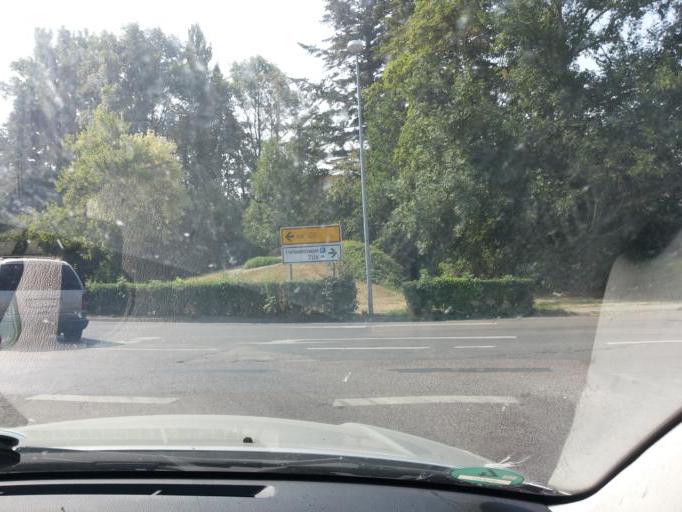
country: DE
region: Bavaria
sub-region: Regierungsbezirk Mittelfranken
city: Bad Windsheim
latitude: 49.5016
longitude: 10.4253
